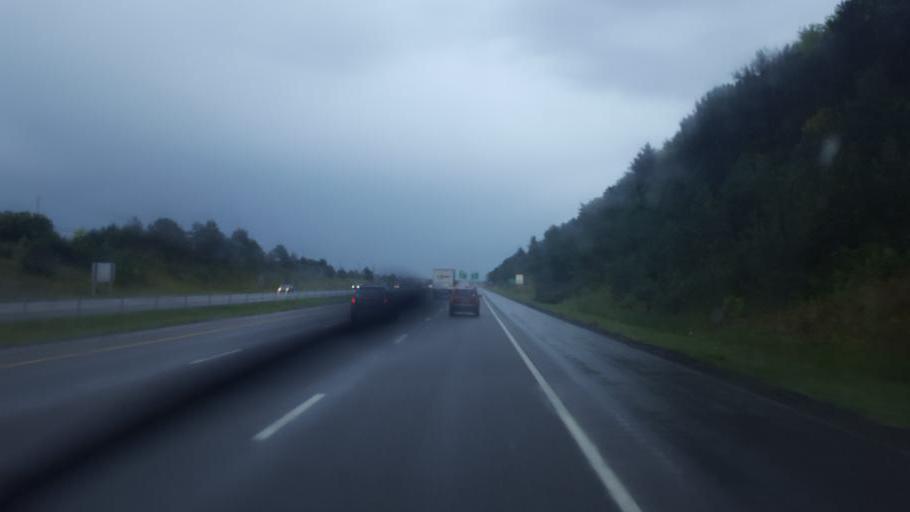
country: US
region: Ohio
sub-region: Summit County
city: Macedonia
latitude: 41.3270
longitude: -81.5164
